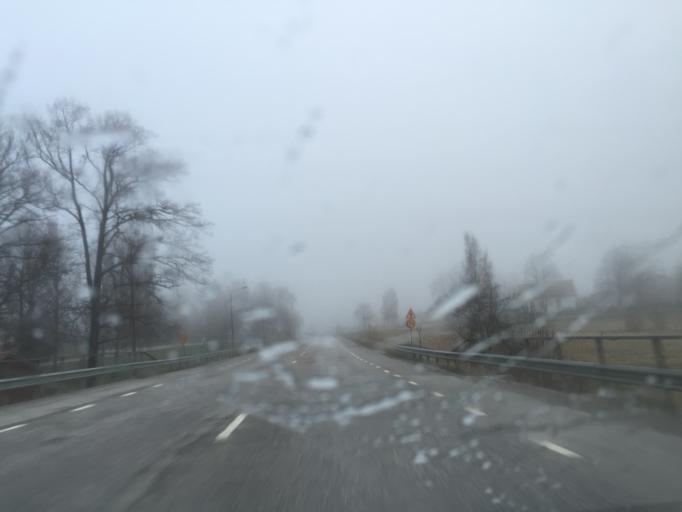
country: SE
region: Soedermanland
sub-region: Nykopings Kommun
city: Olstorp
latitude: 58.8583
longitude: 16.7007
